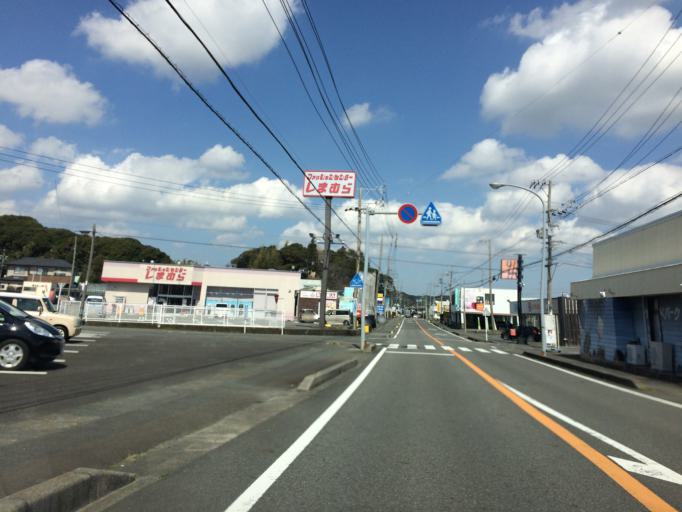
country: JP
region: Shizuoka
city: Sagara
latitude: 34.6881
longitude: 138.1921
